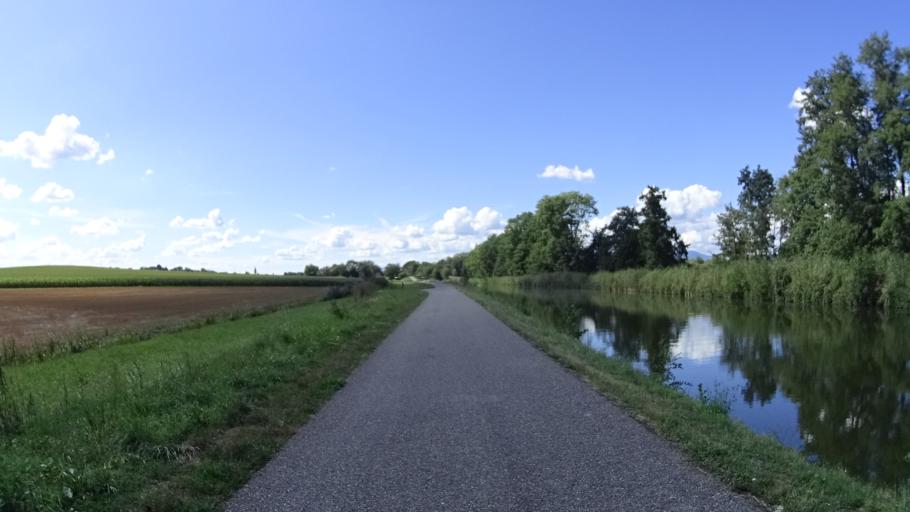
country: FR
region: Alsace
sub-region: Departement du Haut-Rhin
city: Aspach
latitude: 47.6634
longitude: 7.2021
